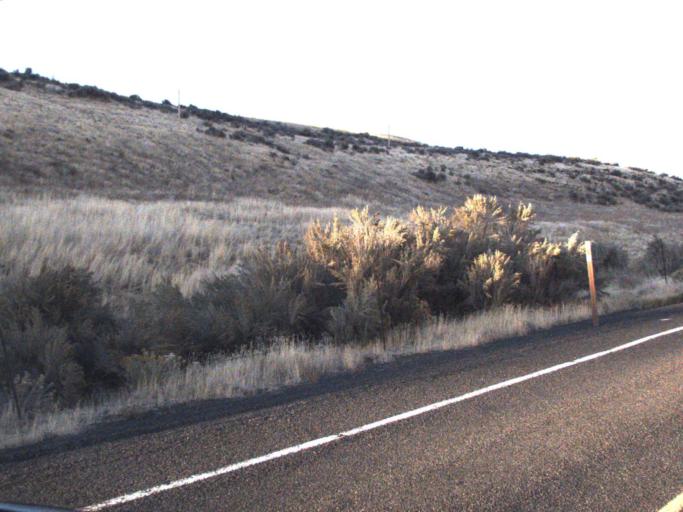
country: US
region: Washington
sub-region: Franklin County
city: Connell
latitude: 46.6876
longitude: -118.5312
